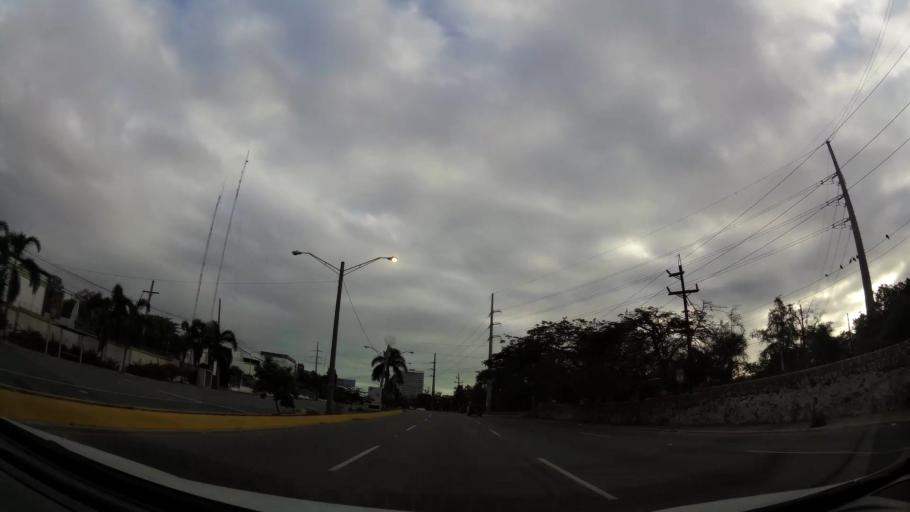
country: DO
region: Nacional
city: Bella Vista
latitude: 18.4336
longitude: -69.9848
